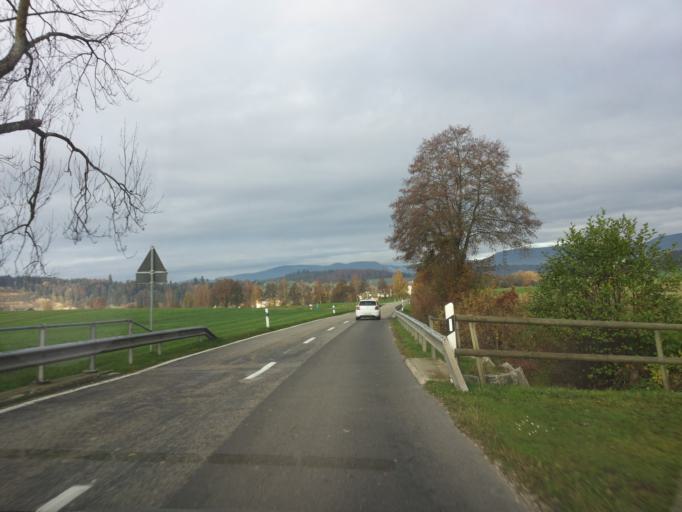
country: CH
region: Bern
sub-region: Oberaargau
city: Roggwil
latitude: 47.2214
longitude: 7.8523
